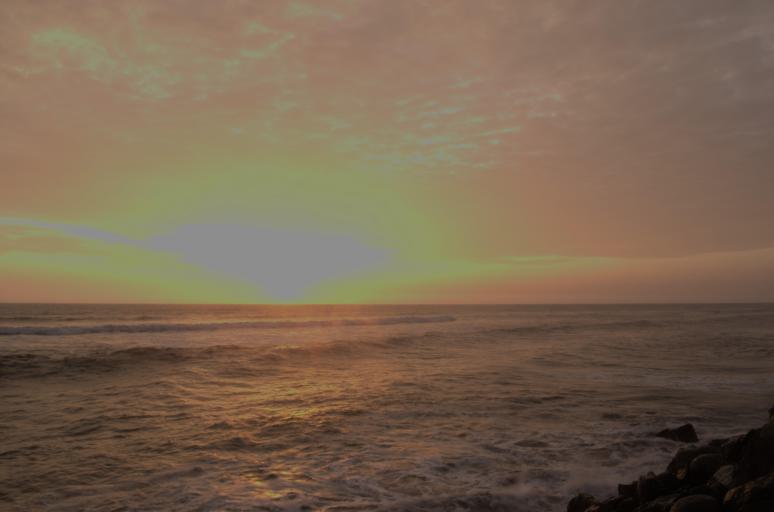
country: PE
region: La Libertad
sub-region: Provincia de Trujillo
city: Buenos Aires
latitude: -8.1340
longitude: -79.0650
